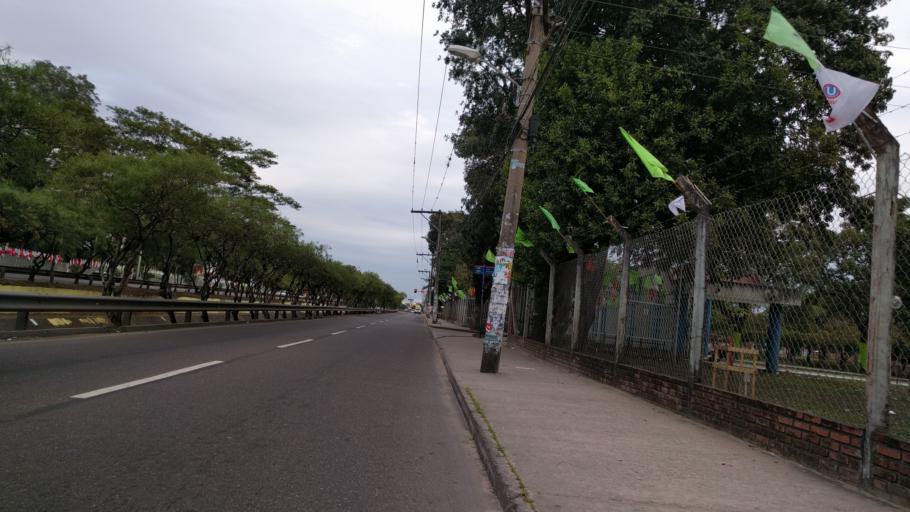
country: BO
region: Santa Cruz
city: Santa Cruz de la Sierra
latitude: -17.7772
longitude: -63.1933
